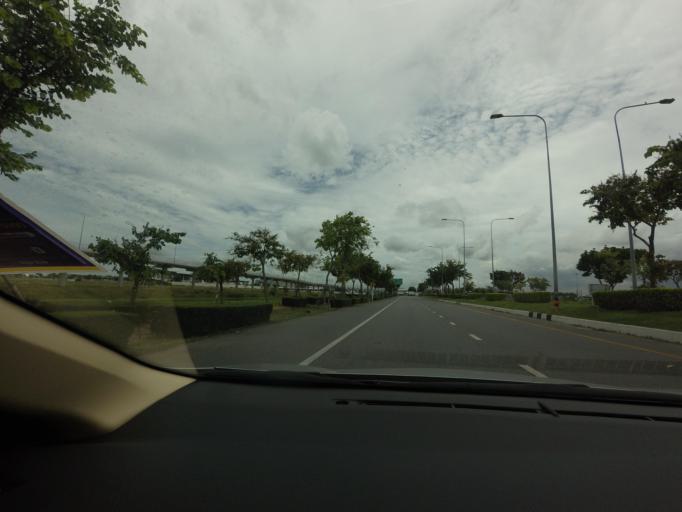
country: TH
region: Bangkok
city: Lat Krabang
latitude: 13.7089
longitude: 100.7719
